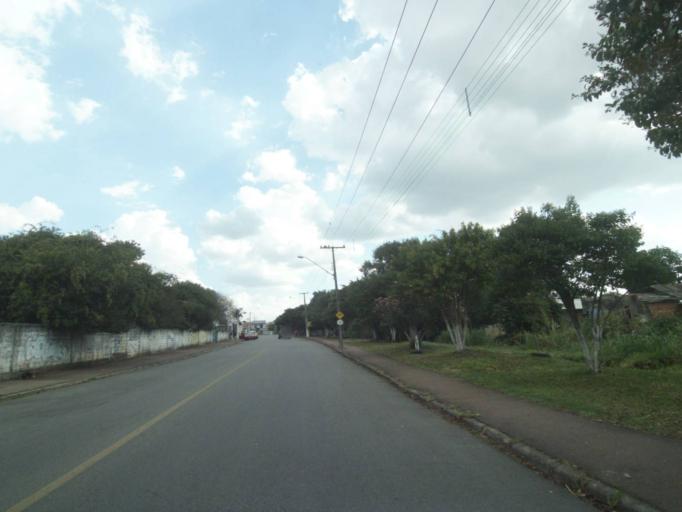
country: BR
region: Parana
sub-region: Sao Jose Dos Pinhais
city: Sao Jose dos Pinhais
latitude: -25.5284
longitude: -49.2700
